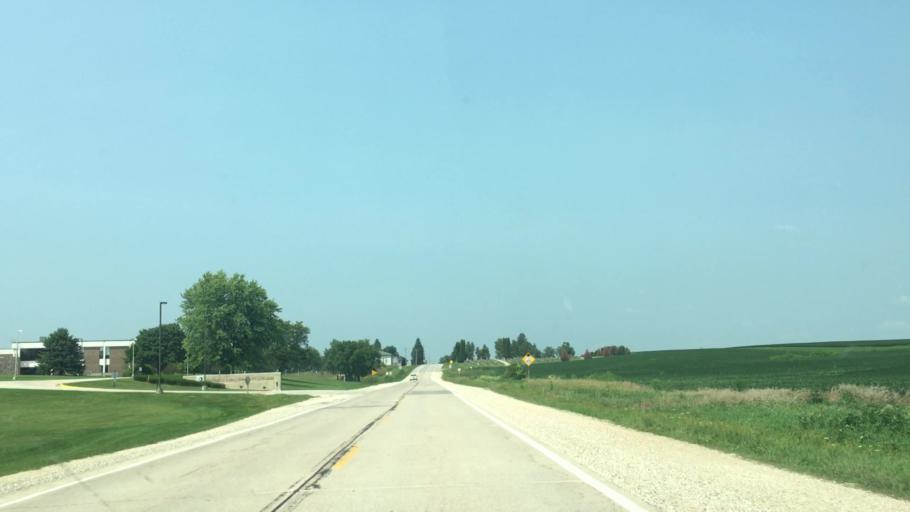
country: US
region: Iowa
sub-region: Winneshiek County
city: Decorah
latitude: 43.1728
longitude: -91.8644
